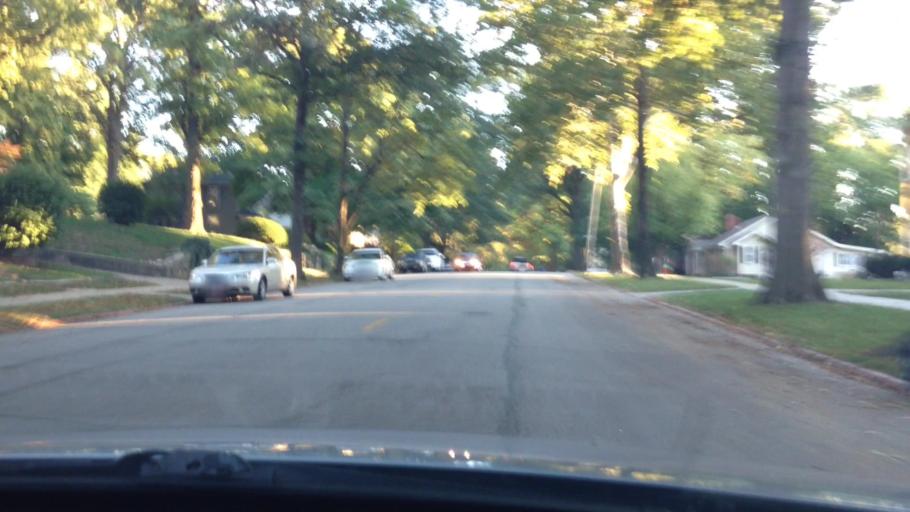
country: US
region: Kansas
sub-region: Leavenworth County
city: Leavenworth
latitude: 39.3057
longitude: -94.9208
